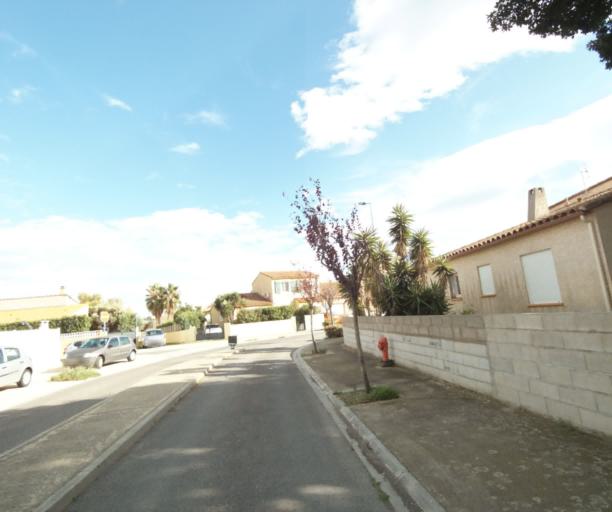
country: FR
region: Languedoc-Roussillon
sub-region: Departement des Pyrenees-Orientales
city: Argelers
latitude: 42.5422
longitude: 3.0185
